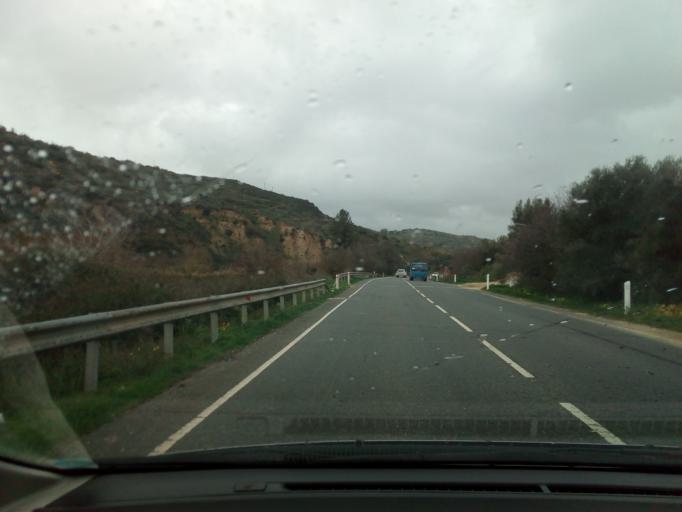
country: CY
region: Pafos
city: Polis
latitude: 34.9567
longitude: 32.4642
